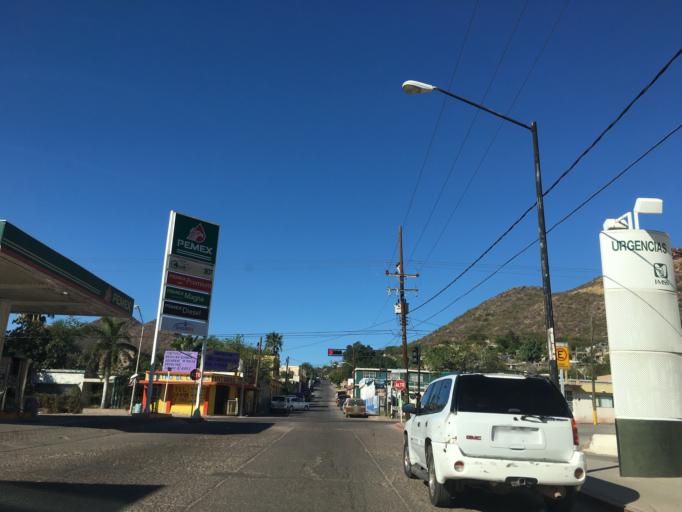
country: MX
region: Sonora
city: Heroica Guaymas
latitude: 27.9178
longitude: -110.9020
